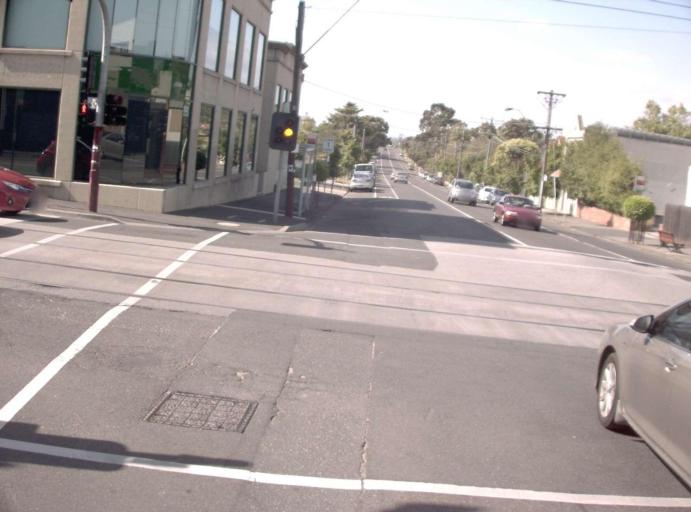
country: AU
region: Victoria
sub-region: Stonnington
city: Malvern East
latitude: -37.8640
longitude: 145.0401
